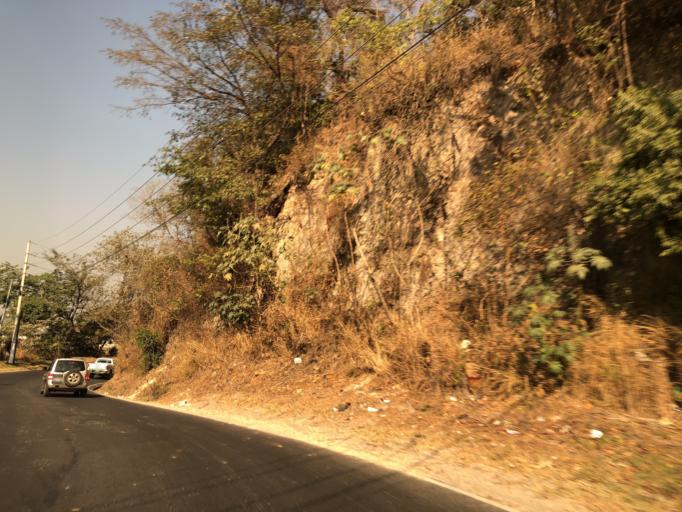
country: GT
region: Guatemala
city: Petapa
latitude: 14.4993
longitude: -90.5409
